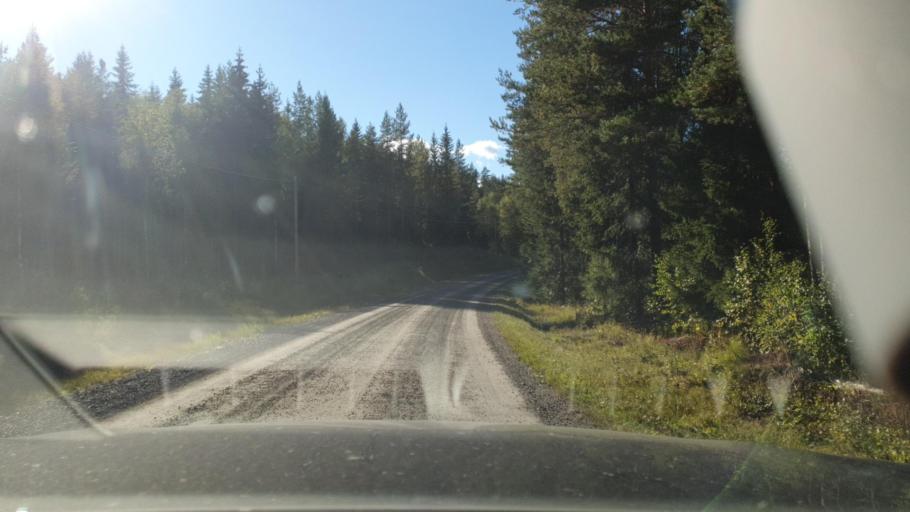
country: SE
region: Vaermland
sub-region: Filipstads Kommun
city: Filipstad
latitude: 59.8136
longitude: 13.9928
